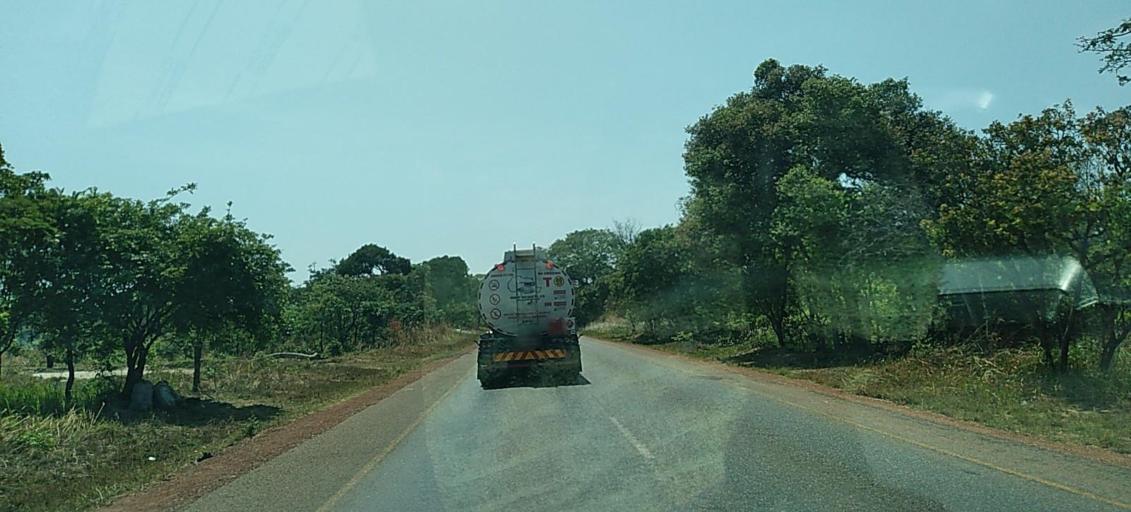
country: ZM
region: North-Western
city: Solwezi
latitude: -12.3620
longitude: 25.9635
